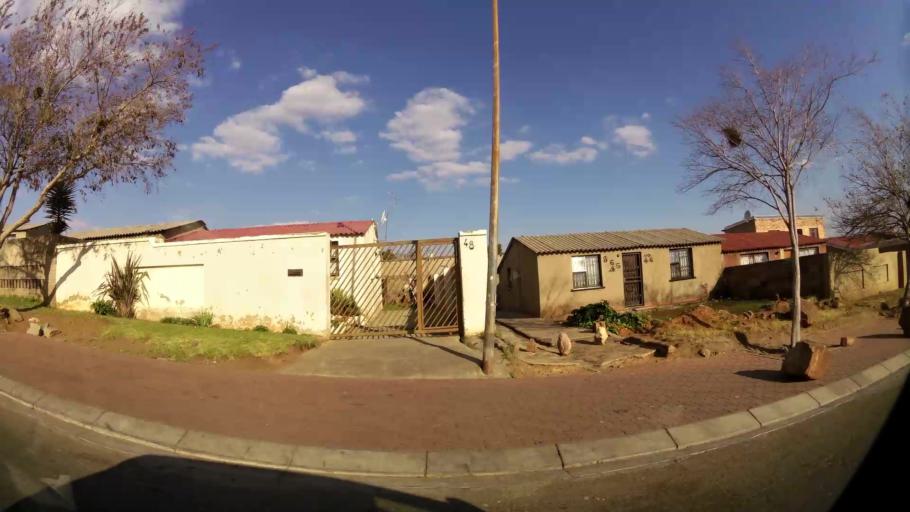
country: ZA
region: Gauteng
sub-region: City of Johannesburg Metropolitan Municipality
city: Roodepoort
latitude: -26.2155
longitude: 27.8858
